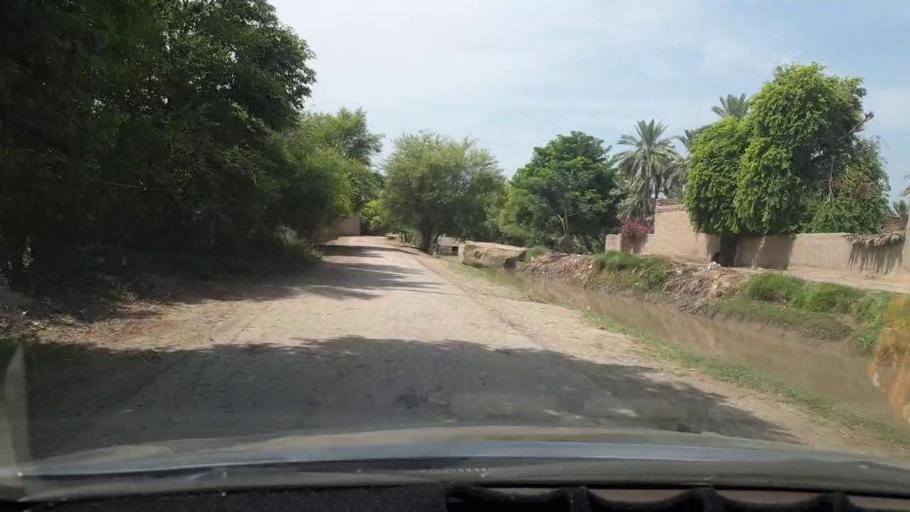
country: PK
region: Sindh
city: Khairpur
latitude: 27.4946
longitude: 68.7450
